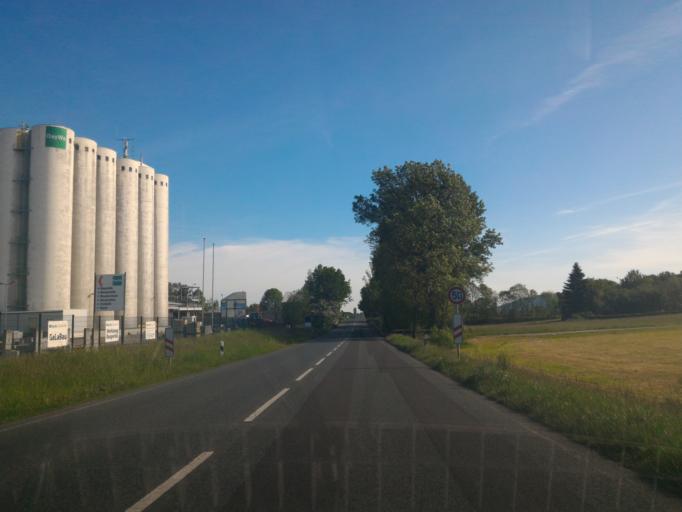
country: DE
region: Saxony
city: Grossschweidnitz
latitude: 51.0505
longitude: 14.6381
